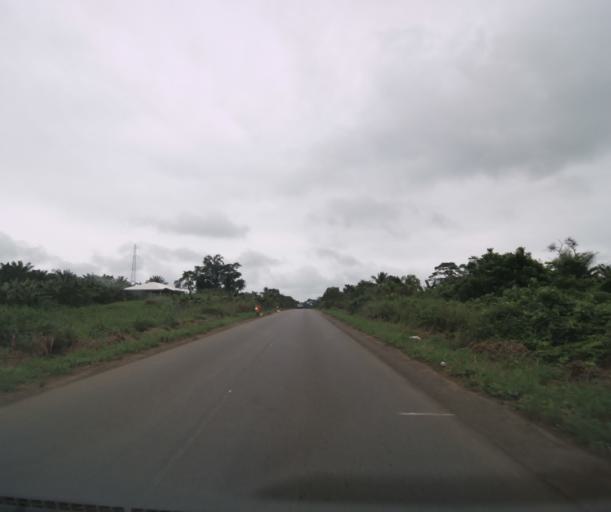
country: CM
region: Littoral
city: Edea
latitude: 3.7282
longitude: 10.1117
